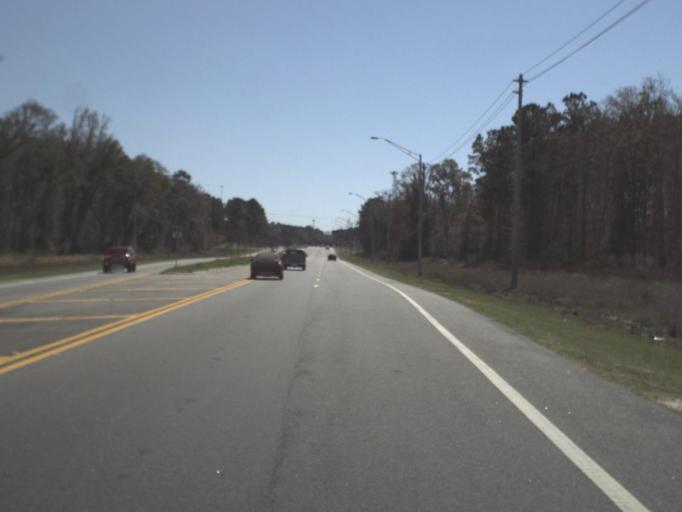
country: US
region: Florida
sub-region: Gadsden County
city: Midway
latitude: 30.4872
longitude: -84.3633
